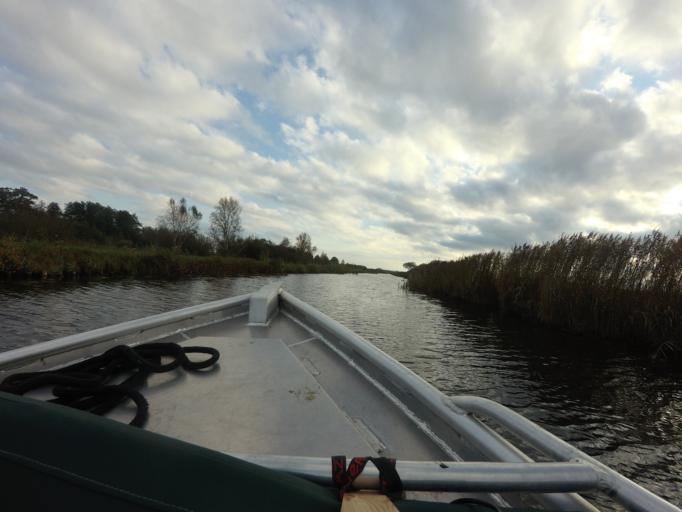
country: NL
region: Overijssel
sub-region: Gemeente Steenwijkerland
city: Blokzijl
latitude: 52.7416
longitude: 5.9757
